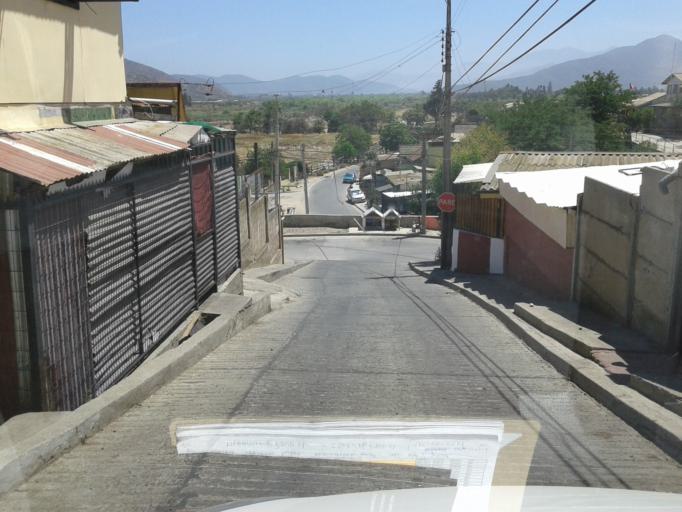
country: CL
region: Valparaiso
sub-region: Provincia de Quillota
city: Quillota
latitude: -32.8727
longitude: -71.2469
